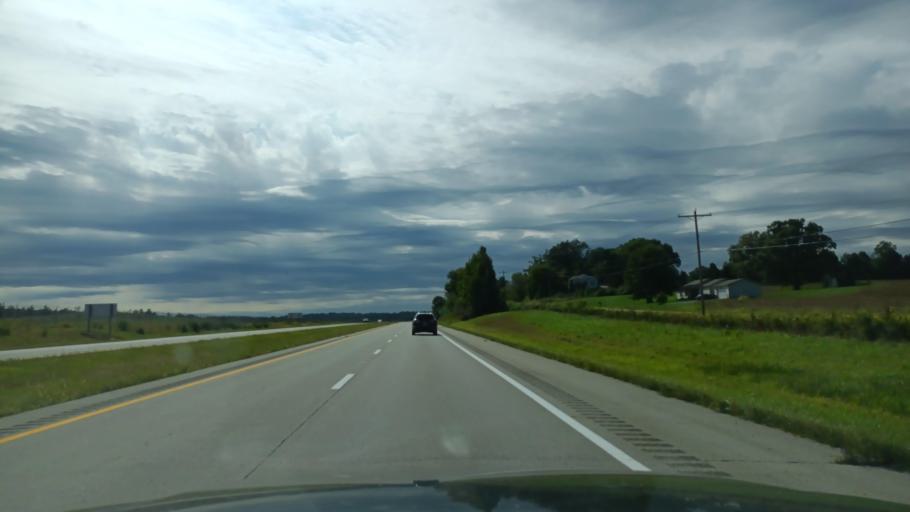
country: US
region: Ohio
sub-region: Athens County
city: Athens
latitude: 39.2159
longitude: -82.2240
